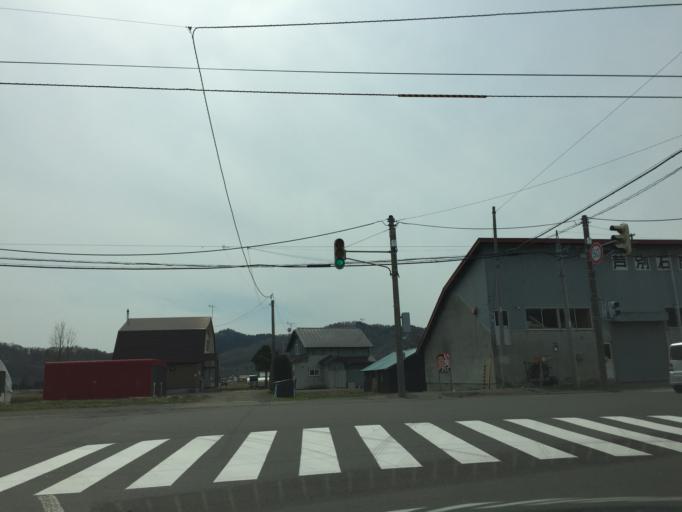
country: JP
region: Hokkaido
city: Ashibetsu
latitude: 43.5435
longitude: 142.1577
